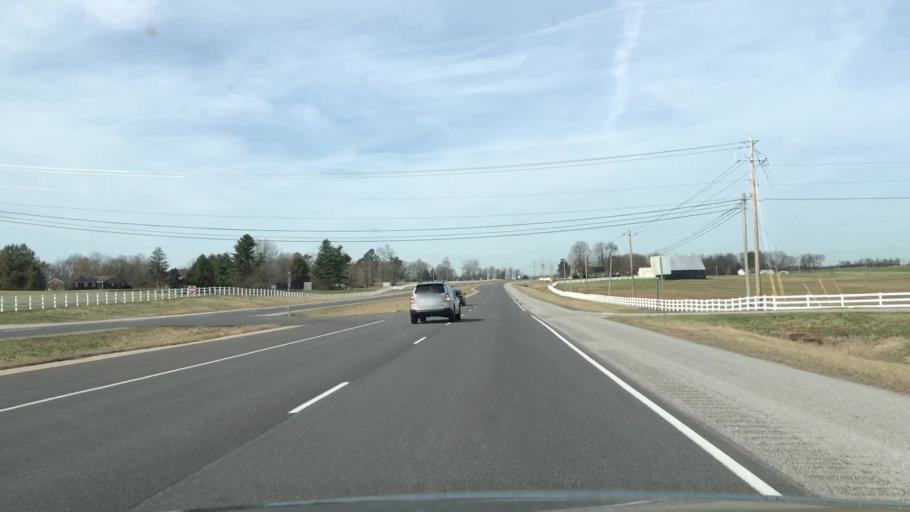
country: US
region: Kentucky
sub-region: Christian County
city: Hopkinsville
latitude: 36.8749
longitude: -87.5503
